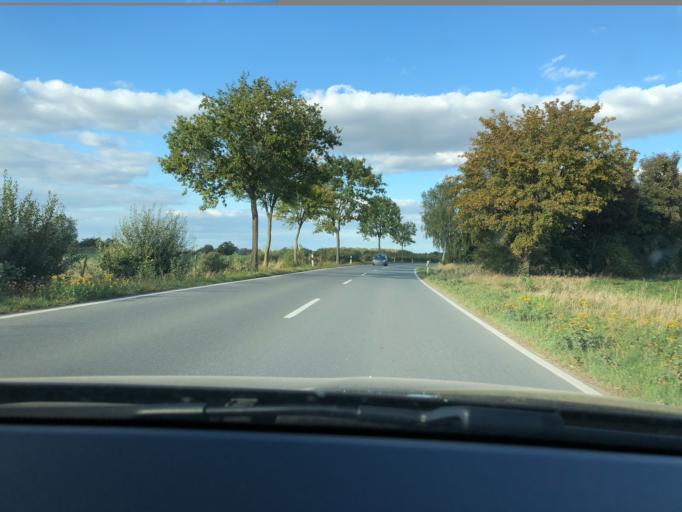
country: DE
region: Lower Saxony
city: Stuhr
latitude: 53.0272
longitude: 8.7865
